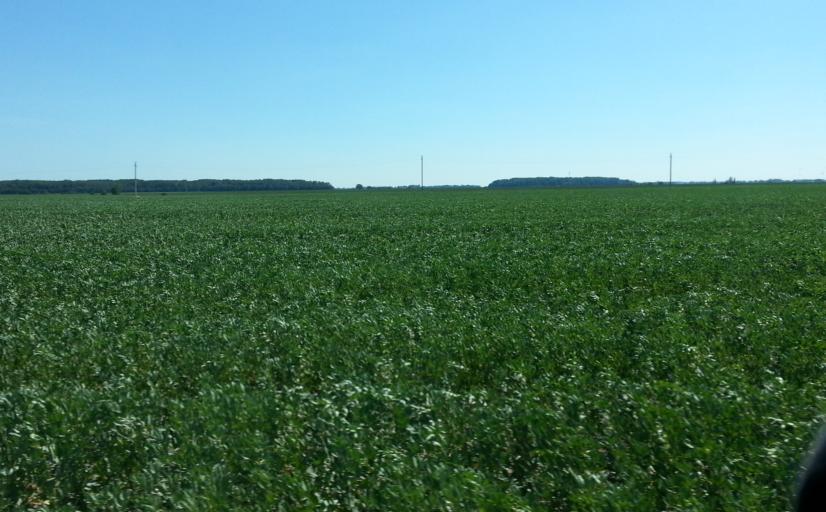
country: LT
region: Panevezys
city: Pasvalys
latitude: 56.2274
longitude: 24.4494
